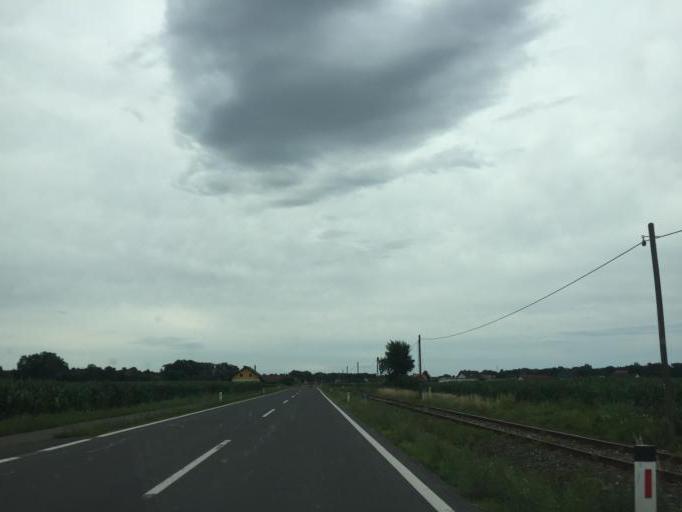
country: SI
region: Apace
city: Apace
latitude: 46.7323
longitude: 15.8924
